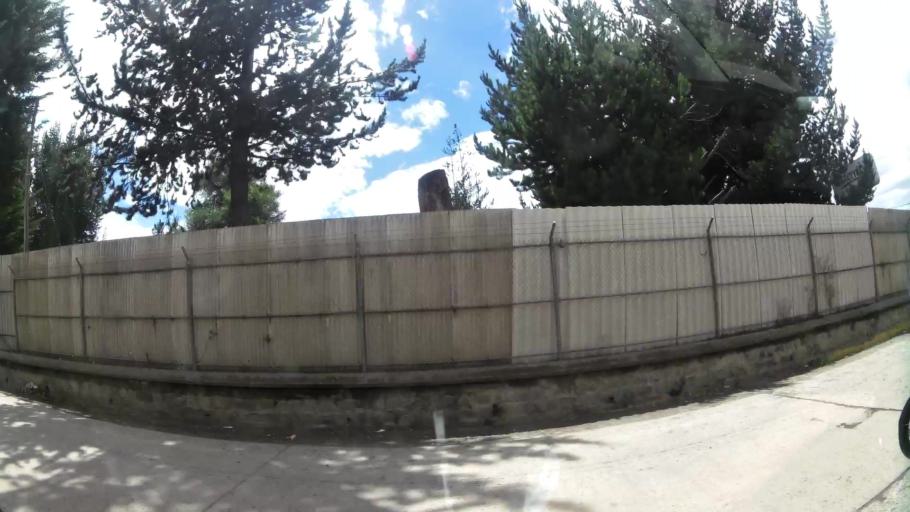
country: EC
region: Pichincha
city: Sangolqui
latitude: -0.3468
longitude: -78.5454
